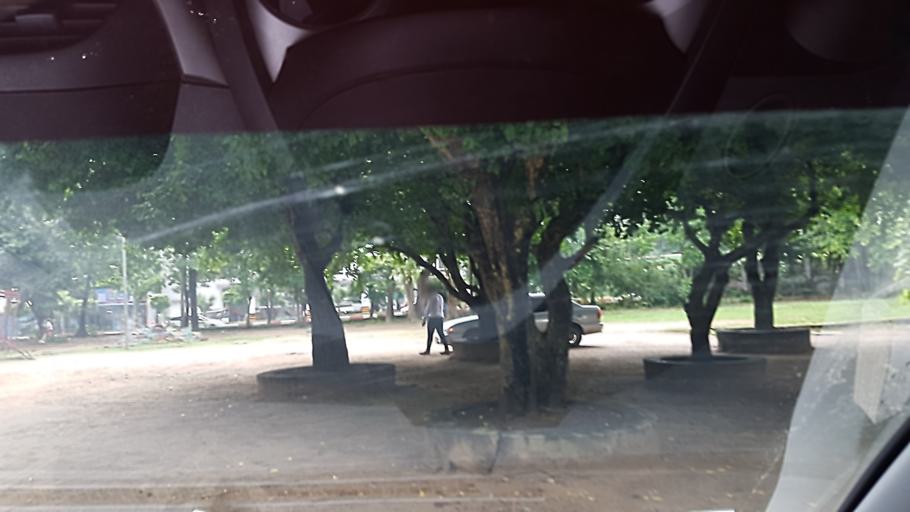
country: MM
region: Yangon
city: Yangon
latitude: 16.7949
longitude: 96.1713
